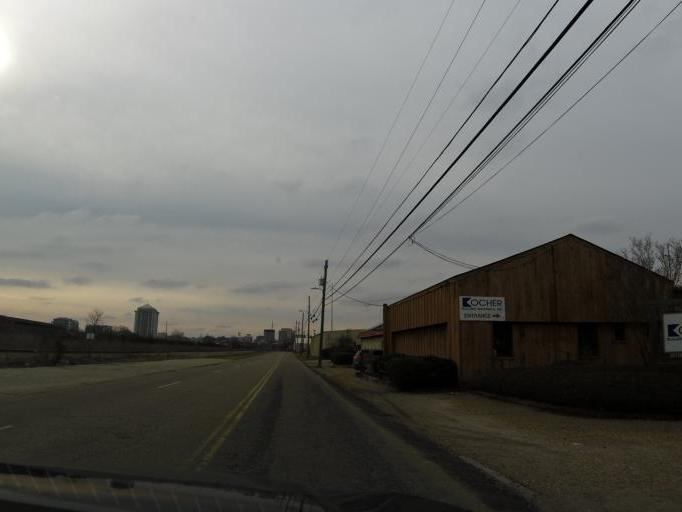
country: US
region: Alabama
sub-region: Montgomery County
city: Montgomery
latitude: 32.3919
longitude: -86.3090
